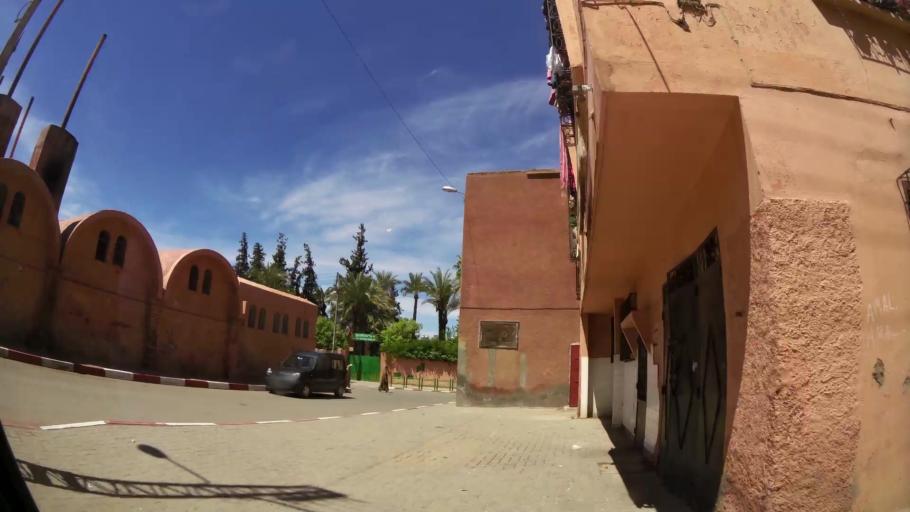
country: MA
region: Marrakech-Tensift-Al Haouz
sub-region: Marrakech
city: Marrakesh
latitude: 31.6569
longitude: -7.9994
